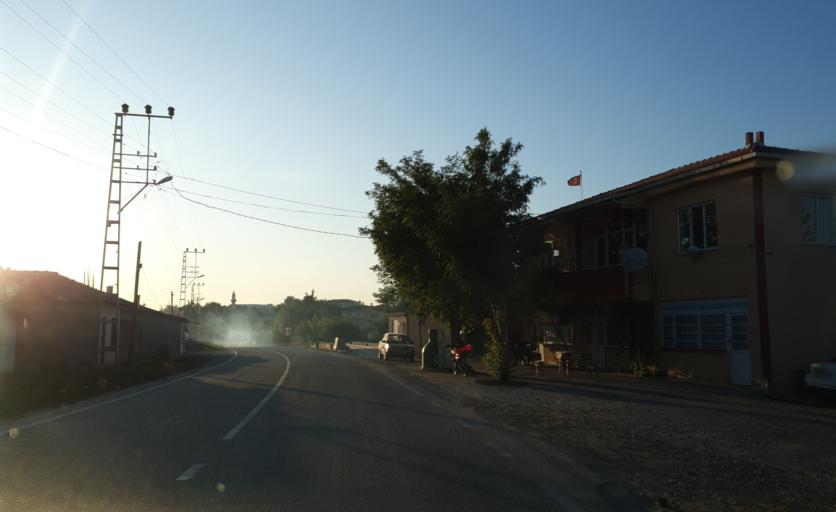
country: TR
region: Tekirdag
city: Beyazkoy
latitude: 41.3354
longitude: 27.7412
